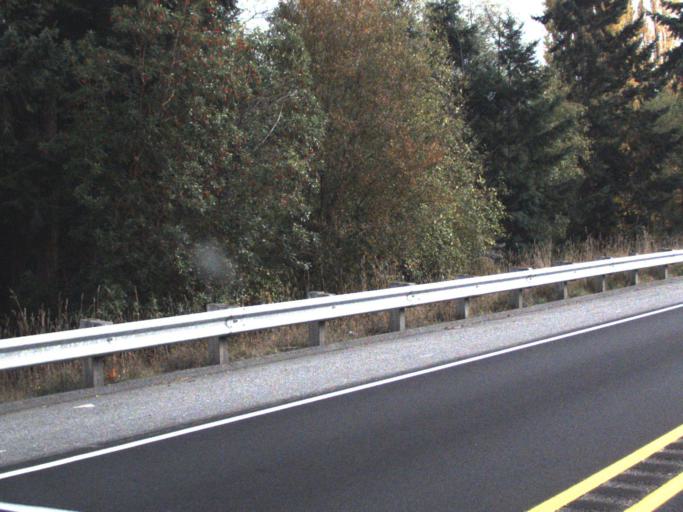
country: US
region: Washington
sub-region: Island County
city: Freeland
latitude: 48.0204
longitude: -122.5545
